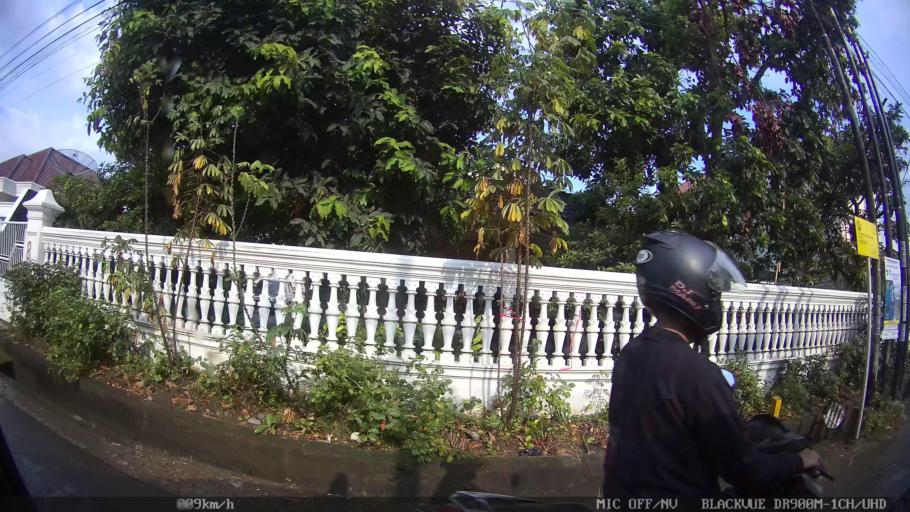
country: ID
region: Lampung
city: Kedaton
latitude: -5.3881
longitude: 105.2946
